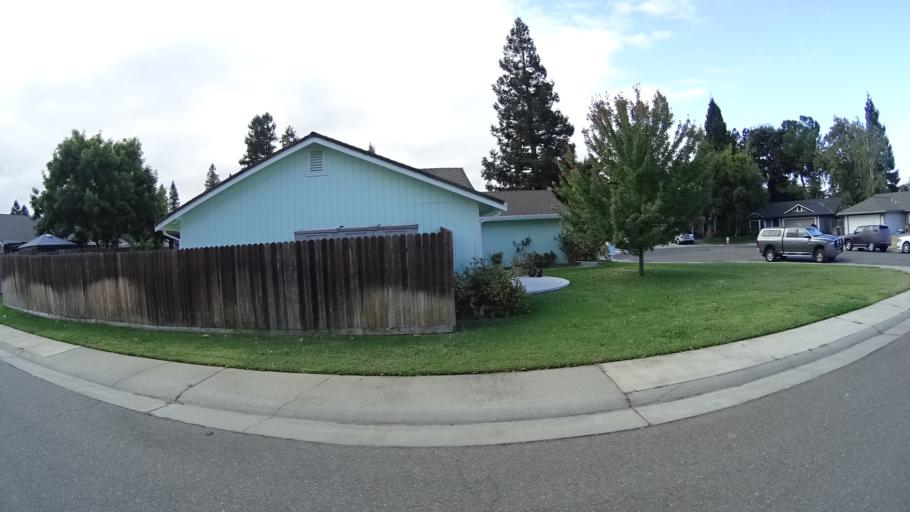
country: US
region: California
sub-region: Sacramento County
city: Laguna
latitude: 38.4215
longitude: -121.4203
